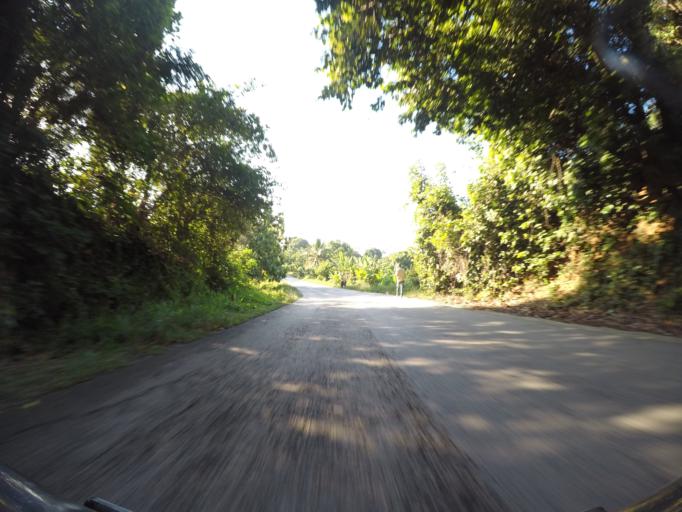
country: TZ
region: Pemba South
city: Mtambile
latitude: -5.3316
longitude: 39.7325
